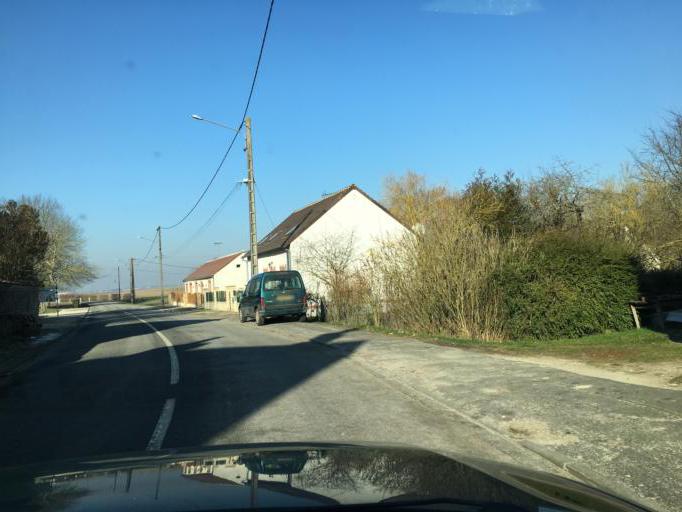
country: FR
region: Centre
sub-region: Departement du Loiret
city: Bricy
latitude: 48.0106
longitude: 1.7389
